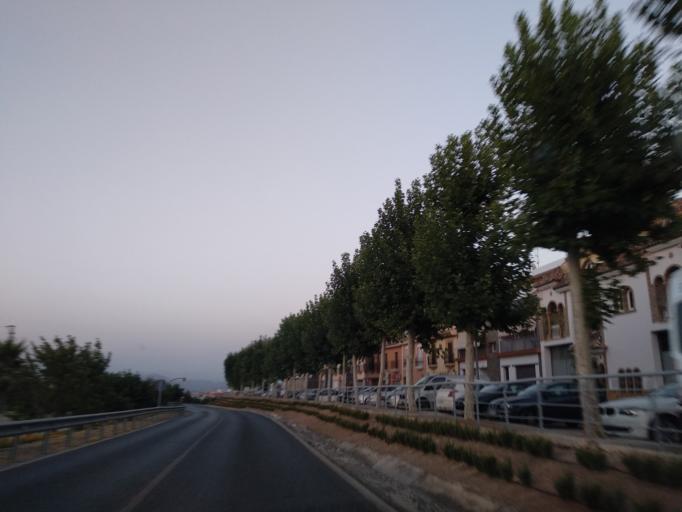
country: ES
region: Andalusia
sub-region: Provincia de Malaga
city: Cartama
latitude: 36.7065
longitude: -4.6398
